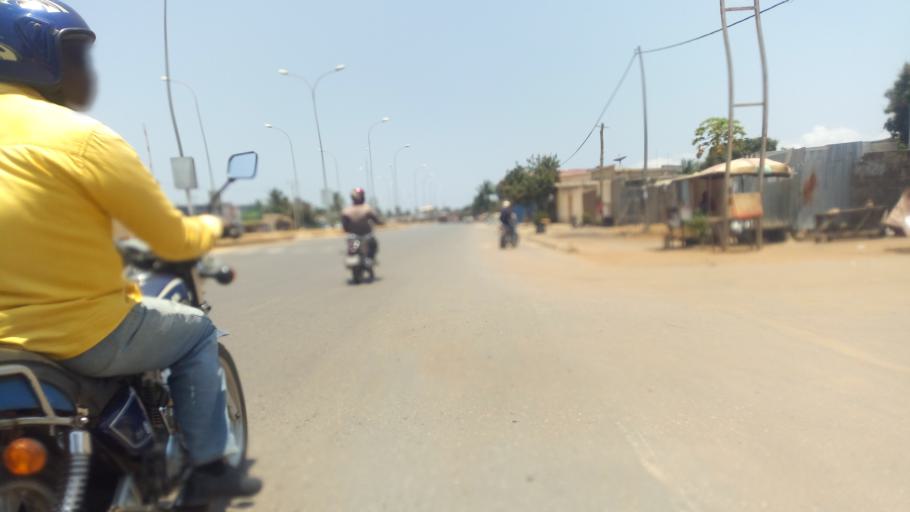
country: TG
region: Maritime
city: Lome
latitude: 6.2138
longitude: 1.1850
